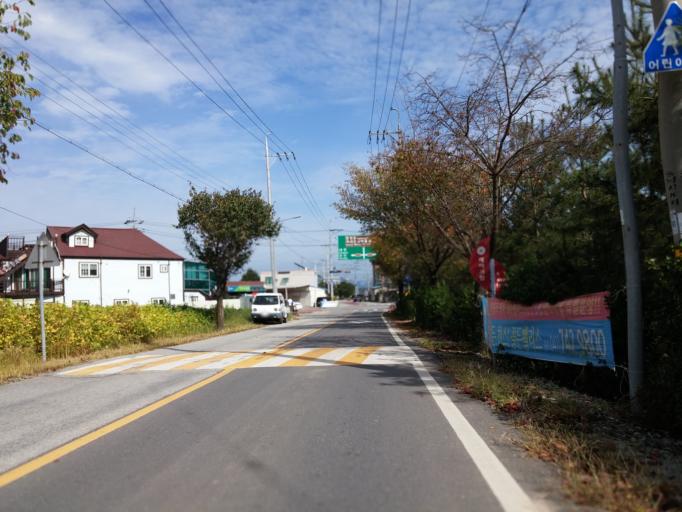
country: KR
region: Chungcheongnam-do
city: Nonsan
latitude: 36.1754
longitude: 127.1285
